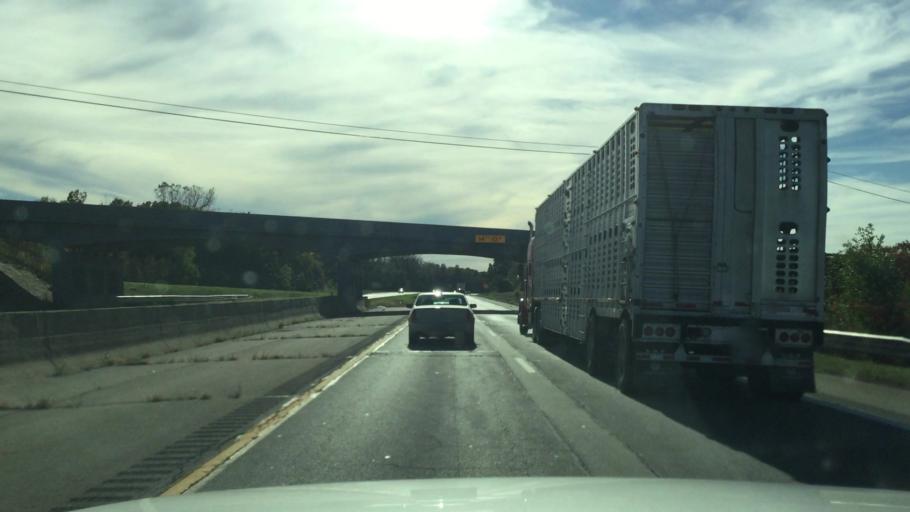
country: US
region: Michigan
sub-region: Jackson County
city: Spring Arbor
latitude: 42.2663
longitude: -84.6196
